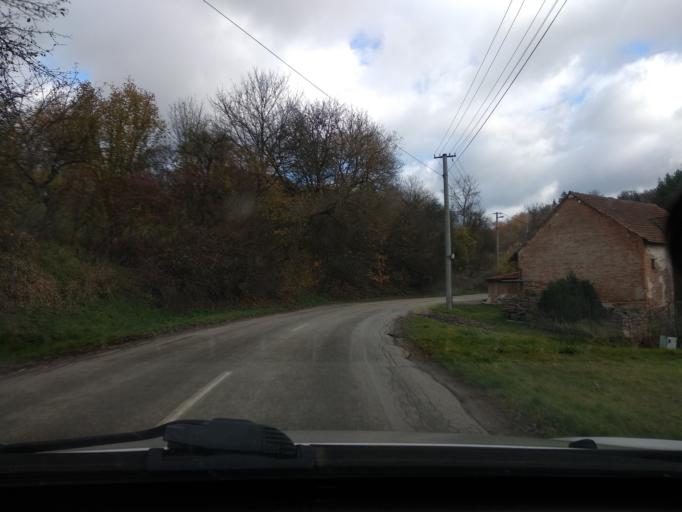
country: CZ
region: South Moravian
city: Drasov
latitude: 49.3743
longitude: 16.4672
